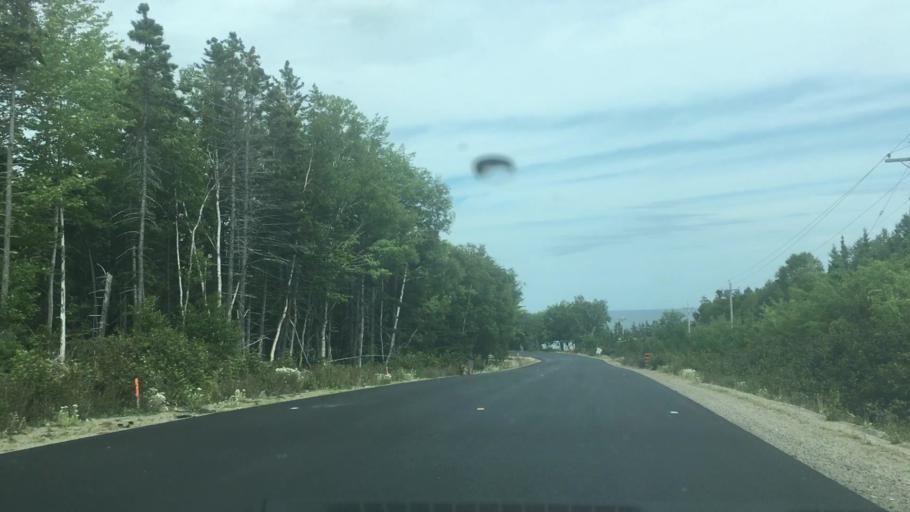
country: CA
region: Nova Scotia
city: Sydney Mines
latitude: 46.5470
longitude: -60.4146
